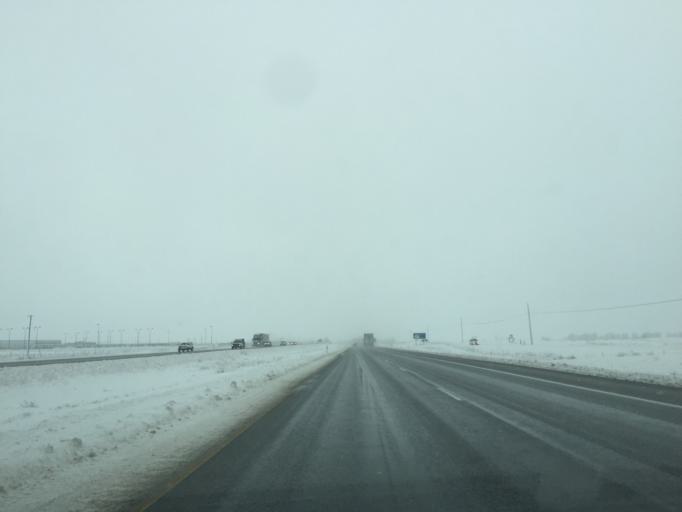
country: US
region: Washington
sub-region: Spokane County
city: Airway Heights
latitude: 47.6011
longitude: -117.5457
